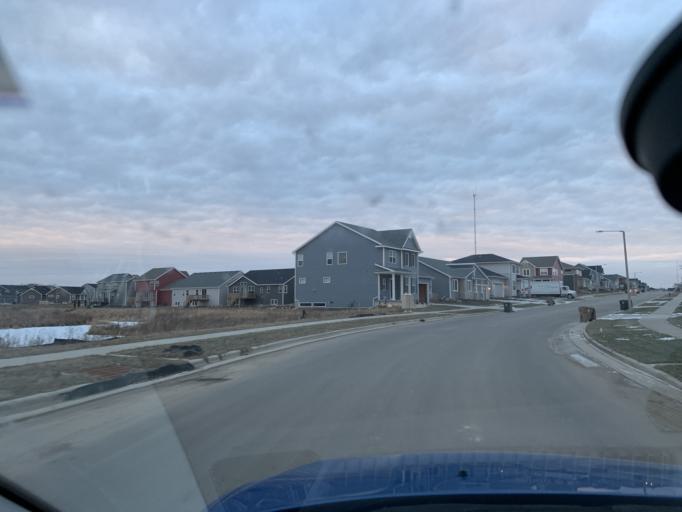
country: US
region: Wisconsin
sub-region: Dane County
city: Verona
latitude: 43.0494
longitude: -89.5590
